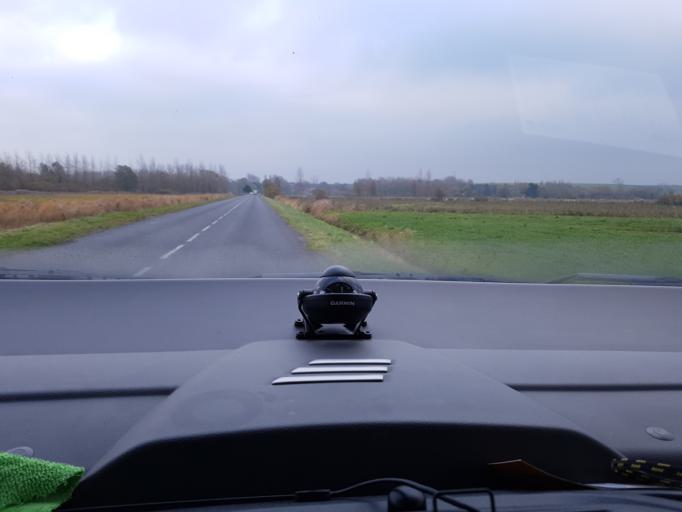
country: FR
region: Picardie
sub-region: Departement de la Somme
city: Cayeux-sur-Mer
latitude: 50.1454
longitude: 1.5114
